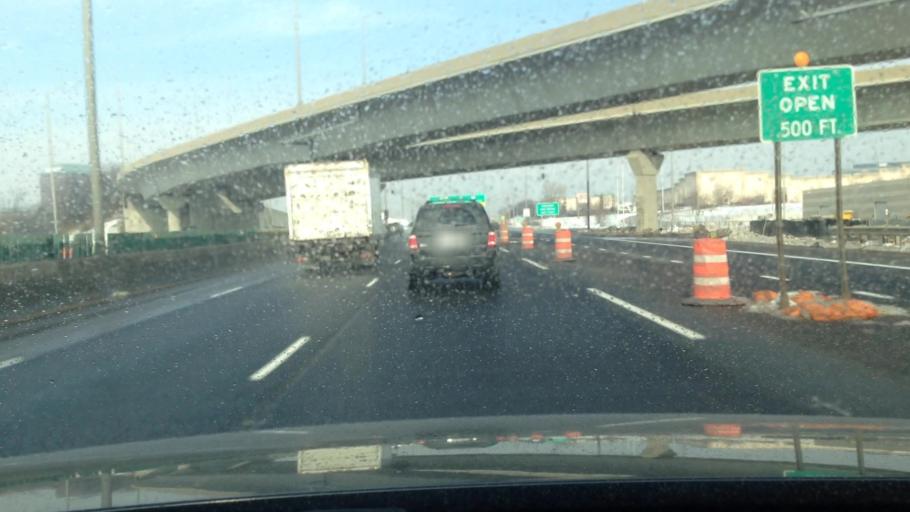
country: US
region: Illinois
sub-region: DuPage County
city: Downers Grove
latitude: 41.8220
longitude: -88.0282
